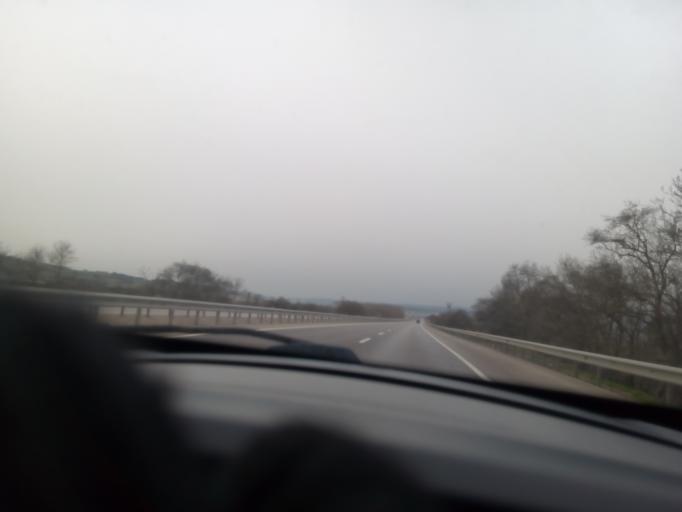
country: TR
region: Balikesir
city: Gobel
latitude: 39.9956
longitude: 28.2127
